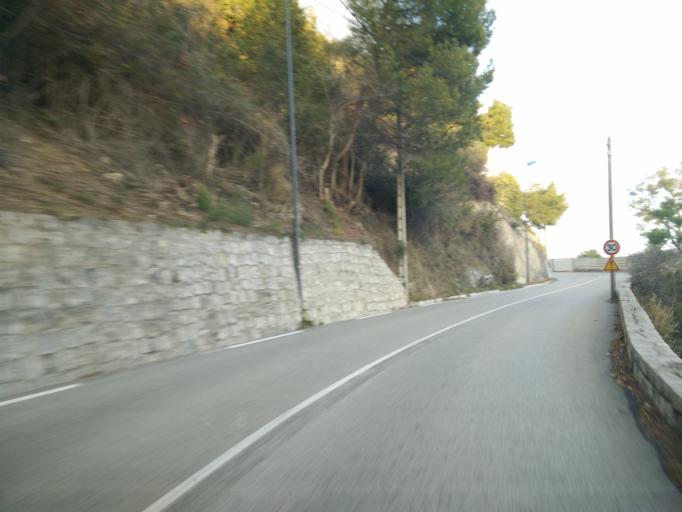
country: FR
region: Provence-Alpes-Cote d'Azur
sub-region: Departement des Alpes-Maritimes
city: Eze
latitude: 43.7320
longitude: 7.3728
